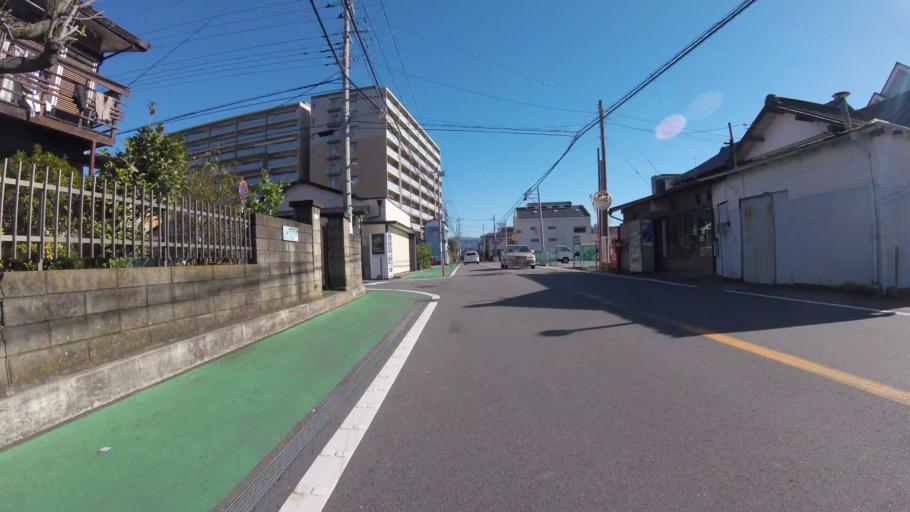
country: JP
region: Shizuoka
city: Mishima
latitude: 35.1199
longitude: 138.9030
